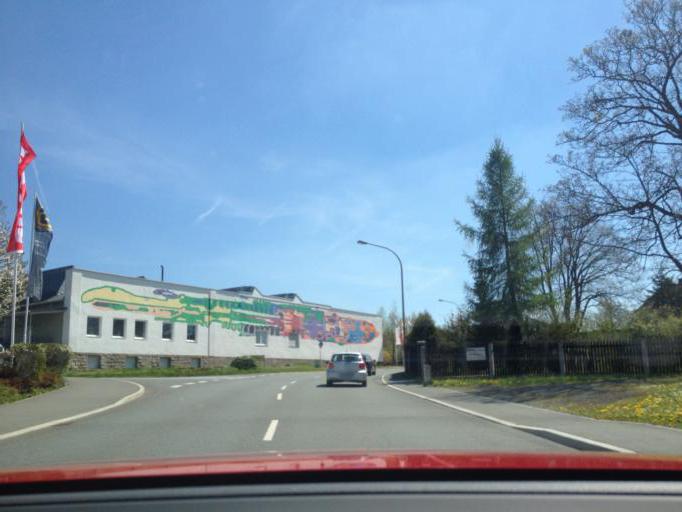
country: DE
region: Bavaria
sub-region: Upper Franconia
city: Schwarzenbach an der Saale
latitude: 50.2191
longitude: 11.9365
